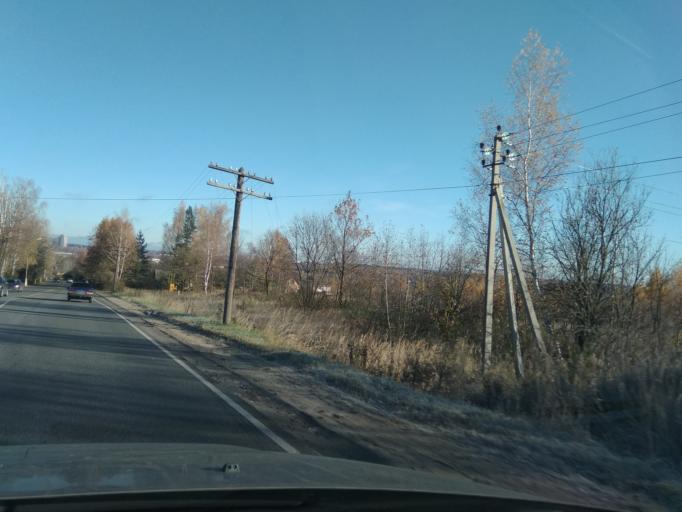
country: RU
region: Moskovskaya
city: Istra
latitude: 55.8832
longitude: 36.8589
